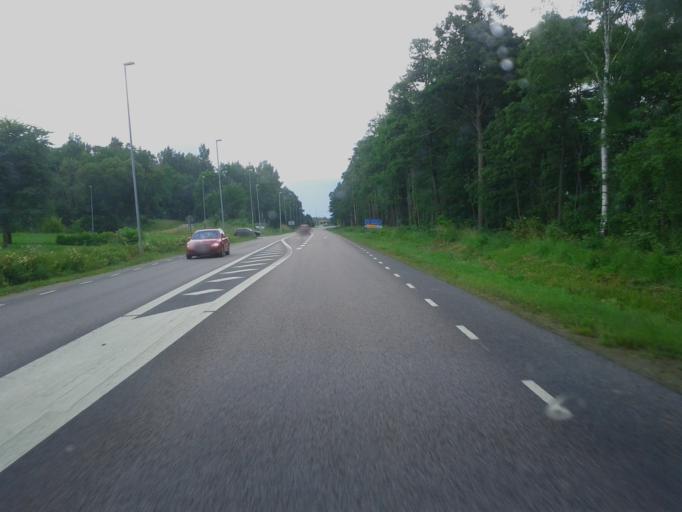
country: SE
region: Vaestmanland
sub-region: Sala Kommun
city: Sala
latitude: 59.9142
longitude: 16.5867
